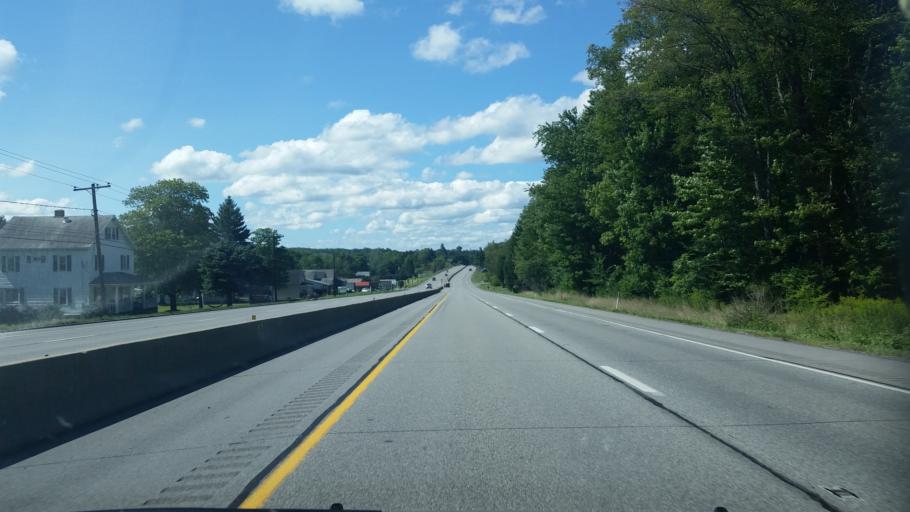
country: US
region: Pennsylvania
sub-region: Cambria County
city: Nanty Glo
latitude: 40.4540
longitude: -78.7823
